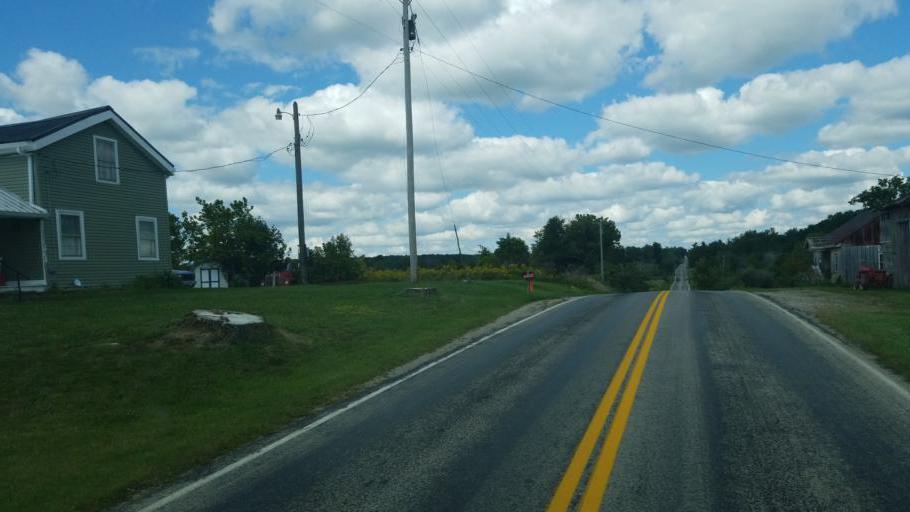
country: US
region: Ohio
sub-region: Ashland County
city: Ashland
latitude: 40.9534
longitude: -82.2819
